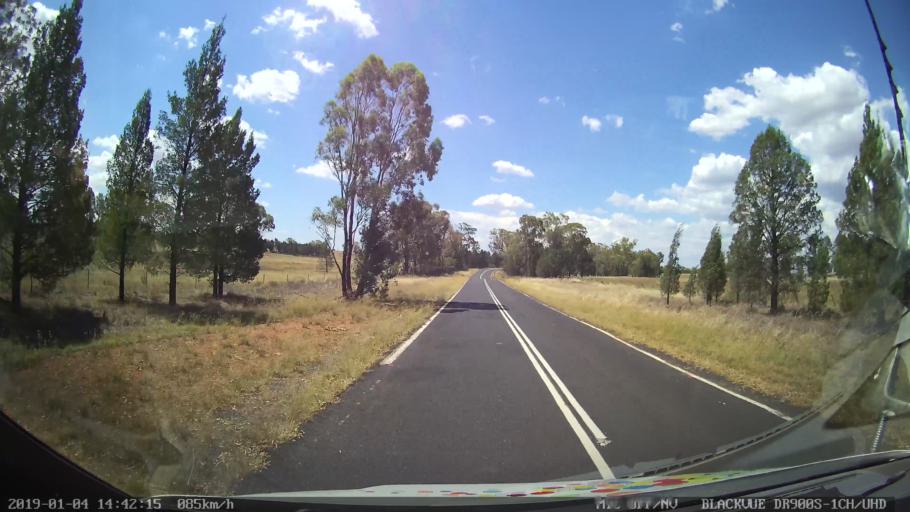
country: AU
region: New South Wales
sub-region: Dubbo Municipality
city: Dubbo
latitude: -32.1304
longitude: 148.6408
